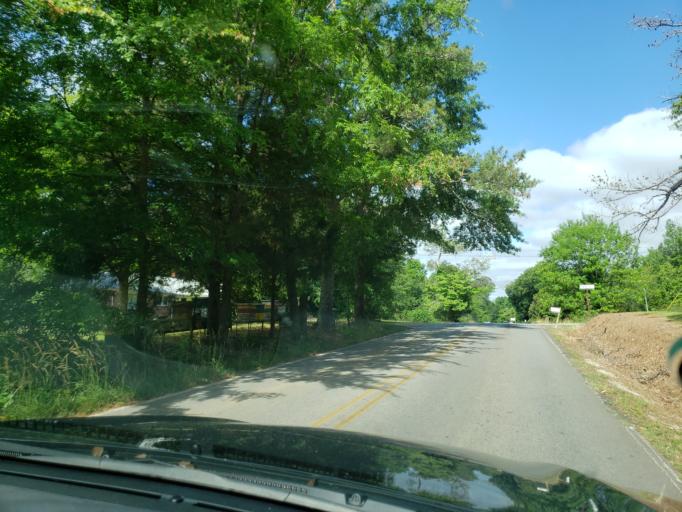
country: US
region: Alabama
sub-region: Calhoun County
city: Weaver
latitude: 33.7515
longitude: -85.8395
